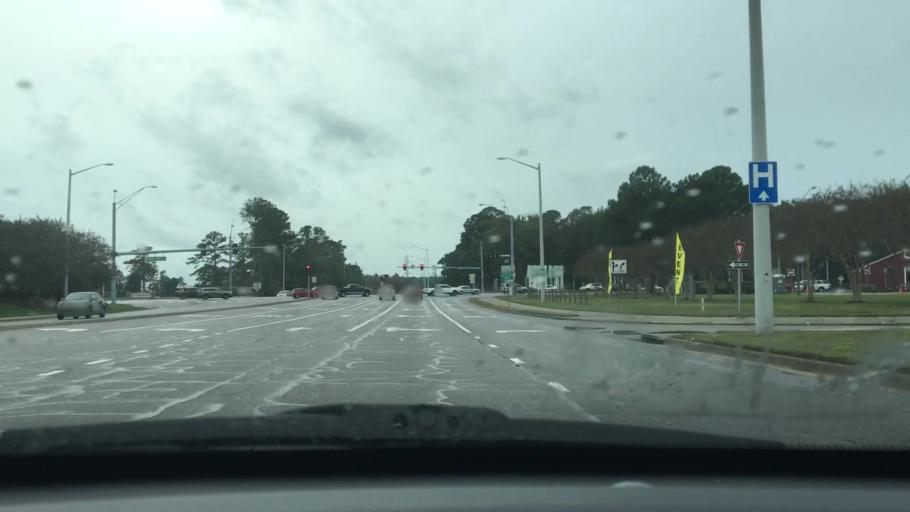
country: US
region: Virginia
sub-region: City of Virginia Beach
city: Virginia Beach
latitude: 36.7762
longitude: -76.0902
